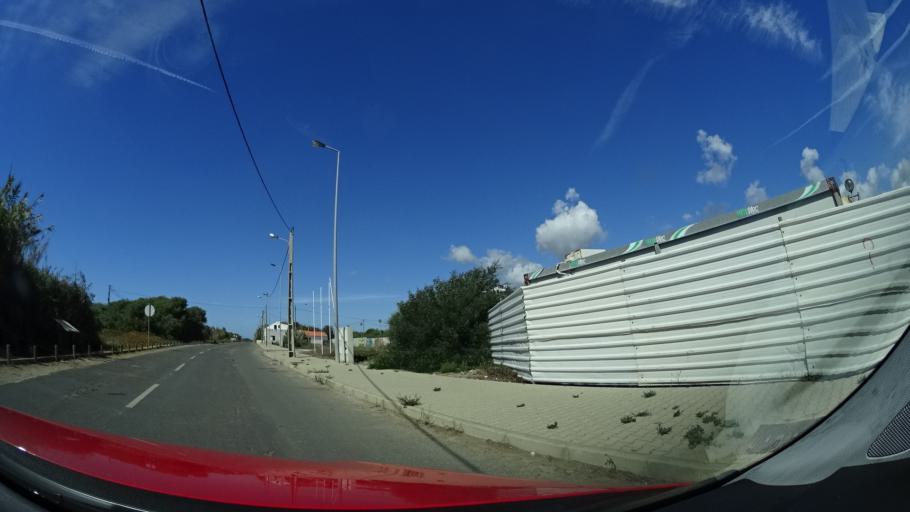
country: PT
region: Beja
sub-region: Odemira
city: Sao Teotonio
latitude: 37.5273
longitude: -8.7842
